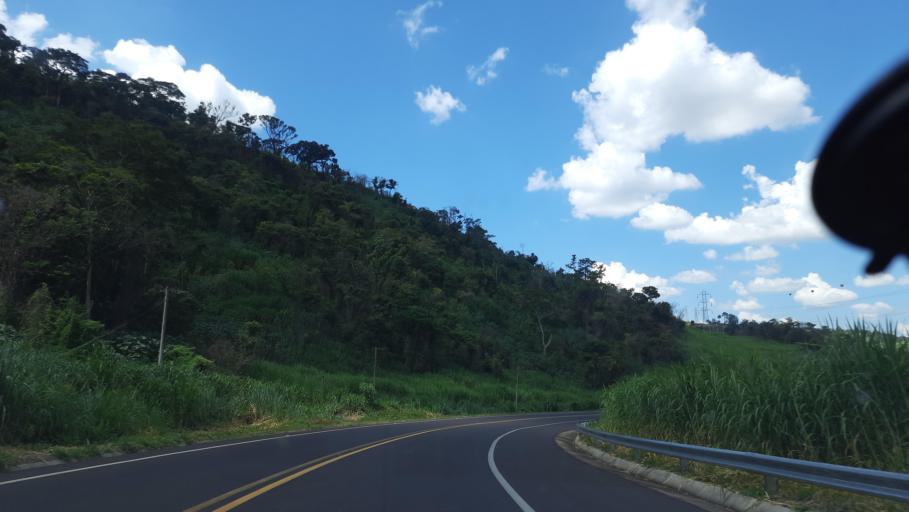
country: BR
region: Sao Paulo
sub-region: Sao Jose Do Rio Pardo
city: Sao Jose do Rio Pardo
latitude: -21.6039
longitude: -46.9597
